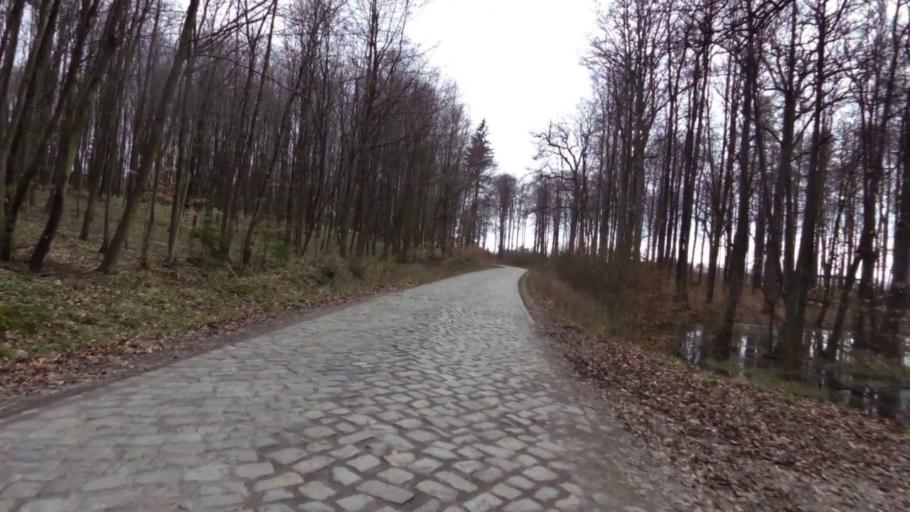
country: PL
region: West Pomeranian Voivodeship
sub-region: Powiat koszalinski
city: Sianow
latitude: 54.2711
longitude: 16.3191
